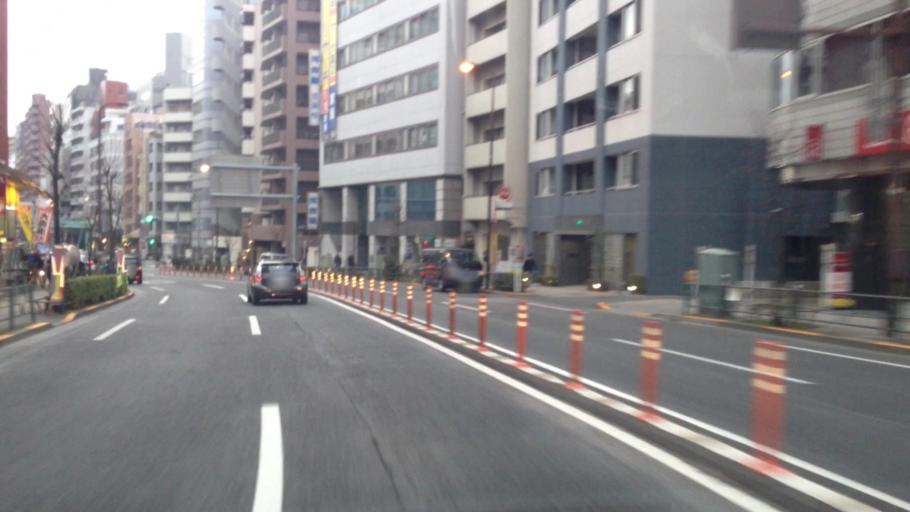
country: JP
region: Tokyo
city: Tokyo
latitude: 35.7249
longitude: 139.7113
